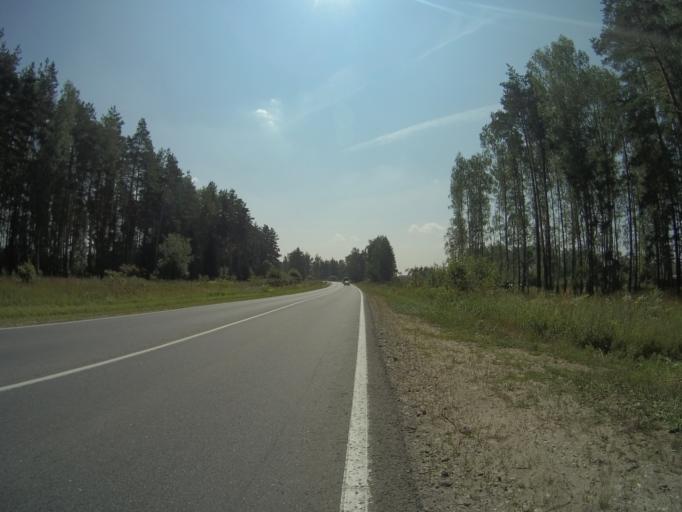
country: RU
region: Vladimir
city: Anopino
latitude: 55.7097
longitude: 40.7292
